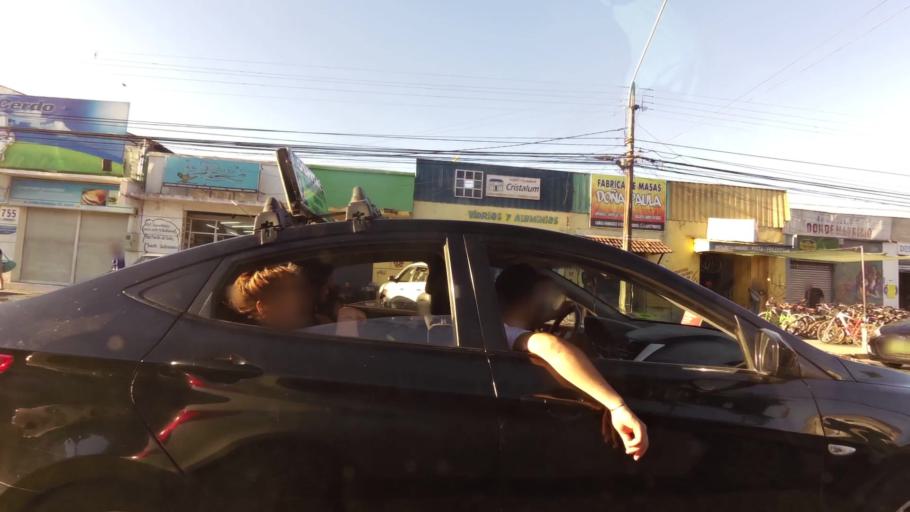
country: CL
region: Maule
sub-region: Provincia de Curico
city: Curico
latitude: -34.9816
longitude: -71.2453
